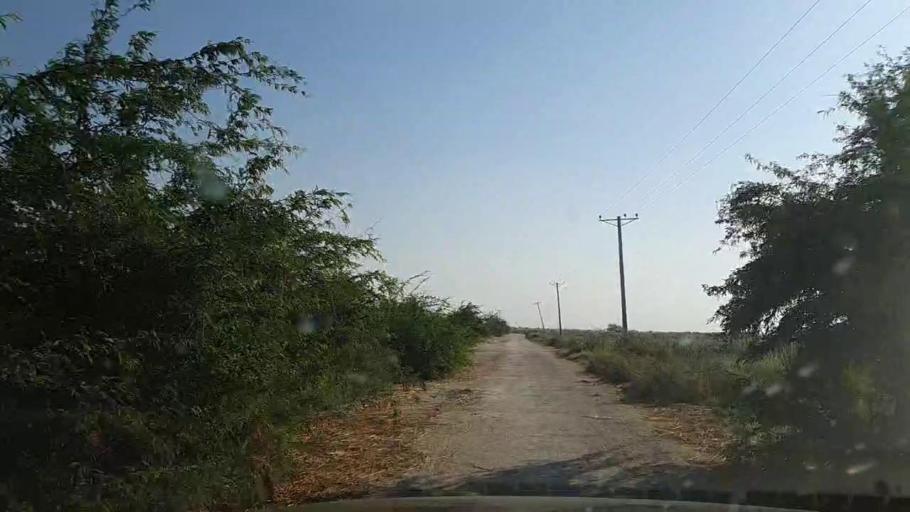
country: PK
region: Sindh
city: Thatta
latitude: 24.6432
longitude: 68.0752
